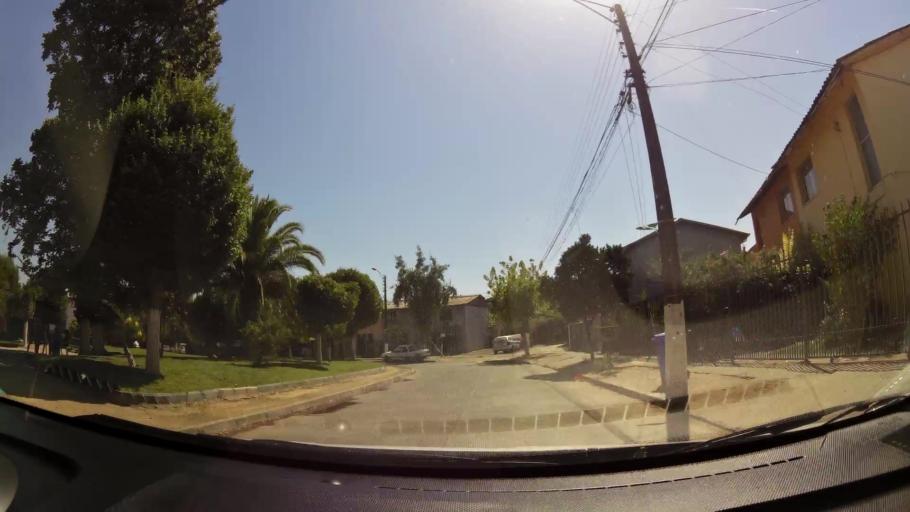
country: CL
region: Maule
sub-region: Provincia de Talca
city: Talca
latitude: -35.4128
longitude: -71.6496
